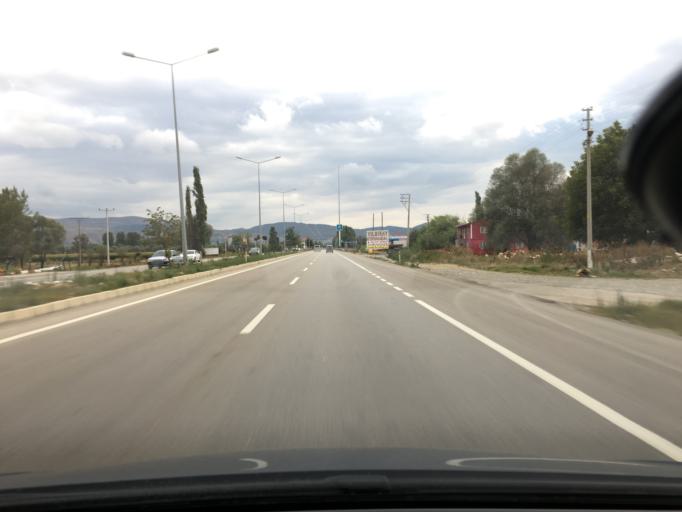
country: TR
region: Afyonkarahisar
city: Sincanli
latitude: 38.7633
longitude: 30.3648
